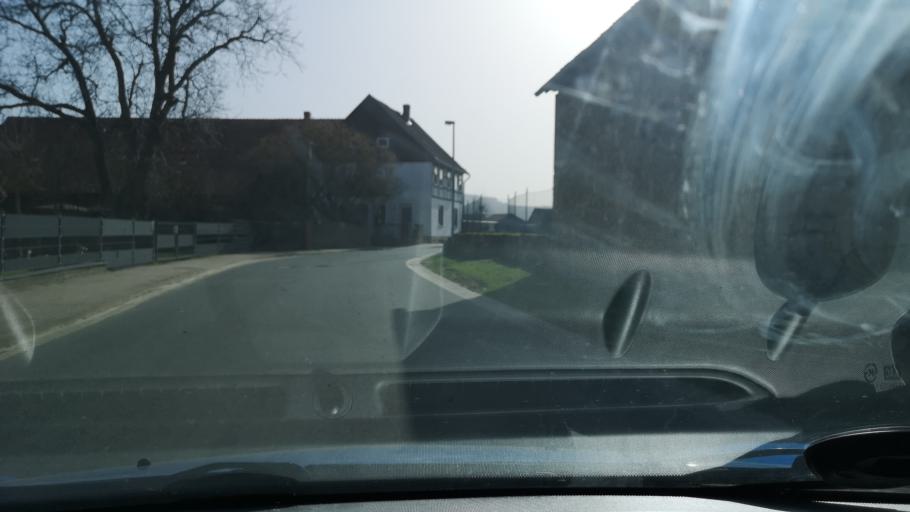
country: DE
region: Lower Saxony
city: Weenzen
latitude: 51.9911
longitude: 9.6515
